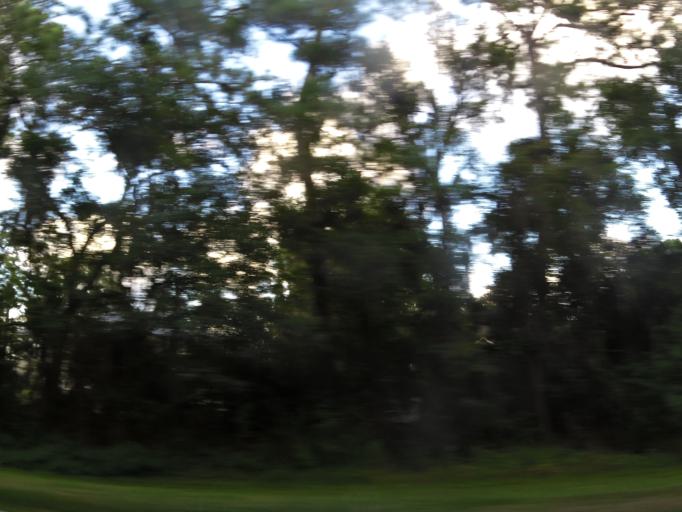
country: US
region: Georgia
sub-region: Glynn County
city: Saint Simon Mills
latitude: 31.1790
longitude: -81.4002
